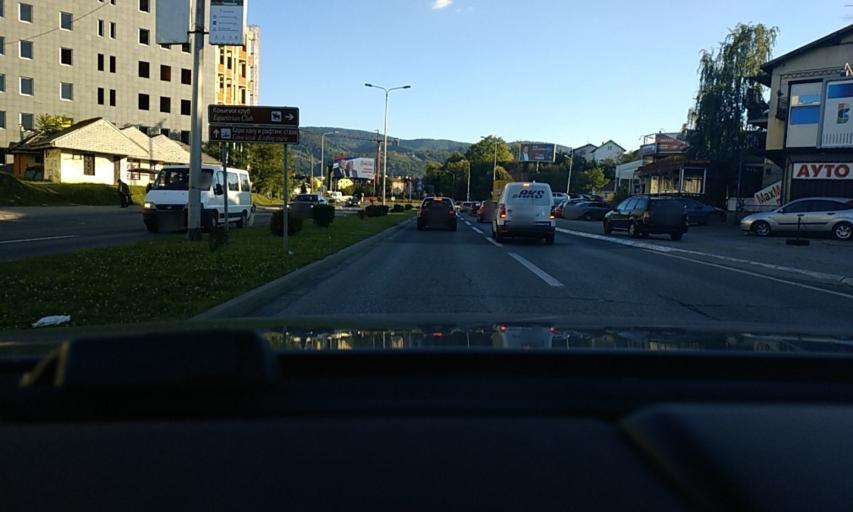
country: BA
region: Republika Srpska
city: Banja Luka
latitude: 44.7725
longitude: 17.1814
